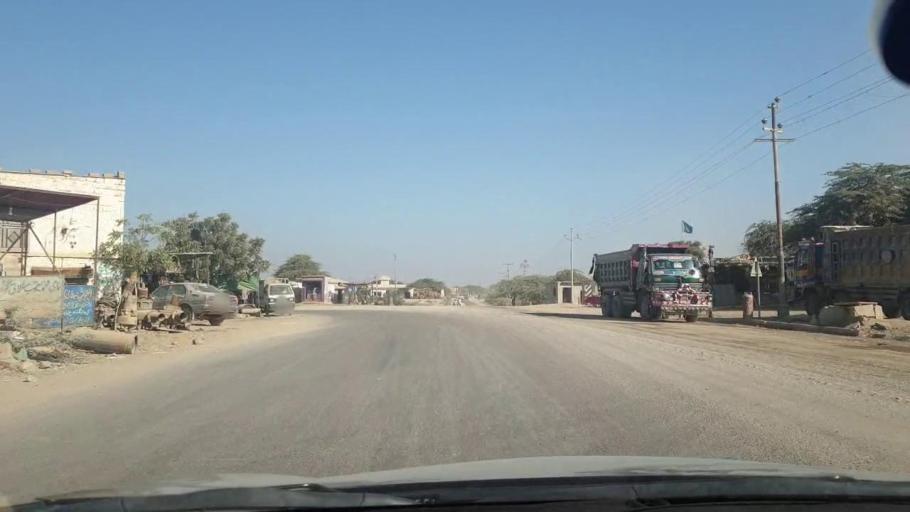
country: PK
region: Sindh
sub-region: Karachi District
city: Karachi
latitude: 25.0906
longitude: 67.0133
